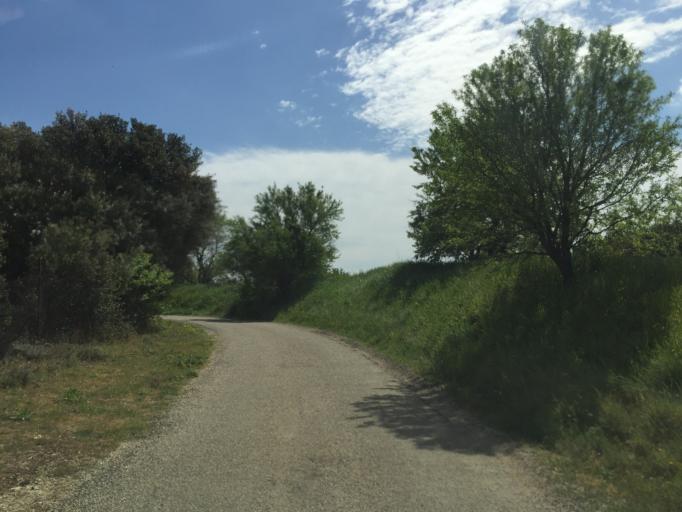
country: FR
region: Provence-Alpes-Cote d'Azur
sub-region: Departement du Vaucluse
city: Courthezon
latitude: 44.0740
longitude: 4.8712
